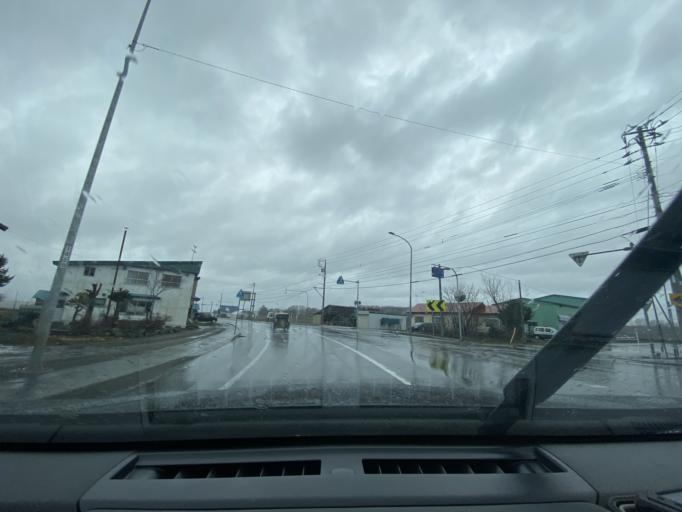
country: JP
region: Hokkaido
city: Fukagawa
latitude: 43.8171
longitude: 142.0001
